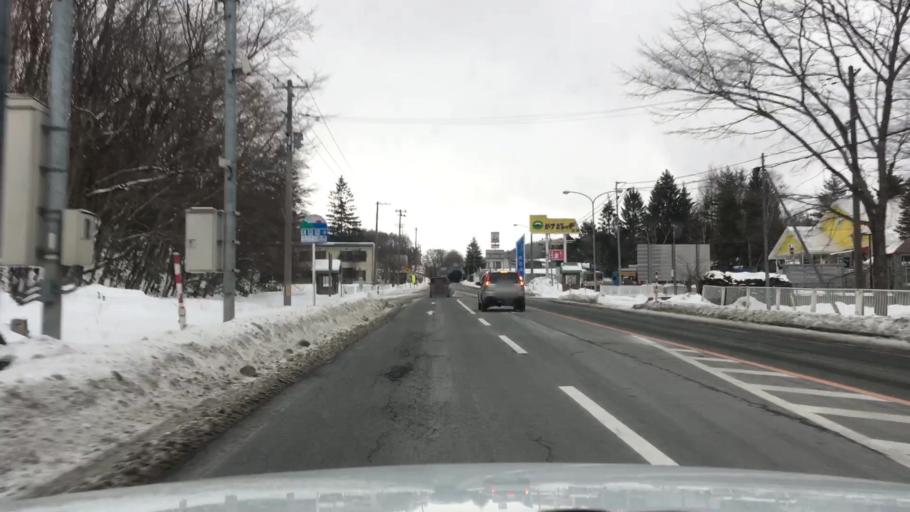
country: JP
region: Iwate
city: Morioka-shi
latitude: 39.6504
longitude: 141.3542
